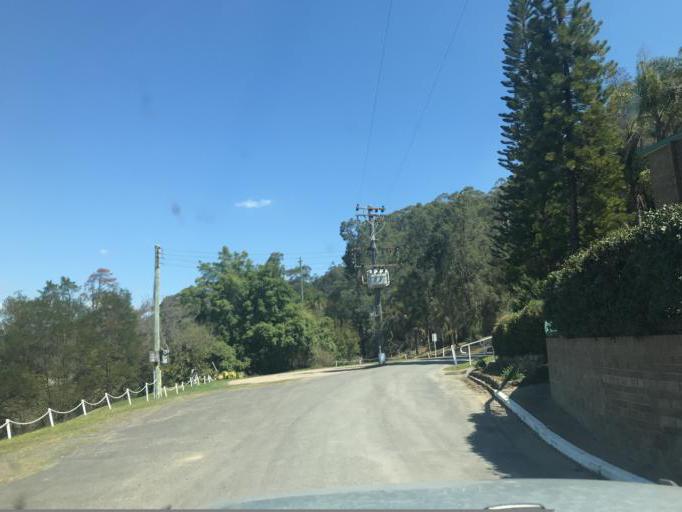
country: AU
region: New South Wales
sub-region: Hawkesbury
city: Pitt Town
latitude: -33.4223
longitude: 150.8954
